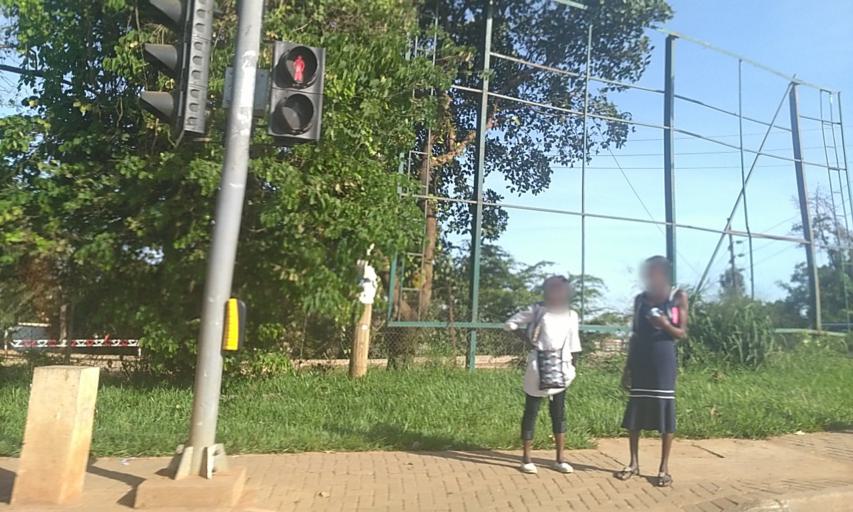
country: UG
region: Central Region
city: Kampala Central Division
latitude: 0.3431
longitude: 32.5957
